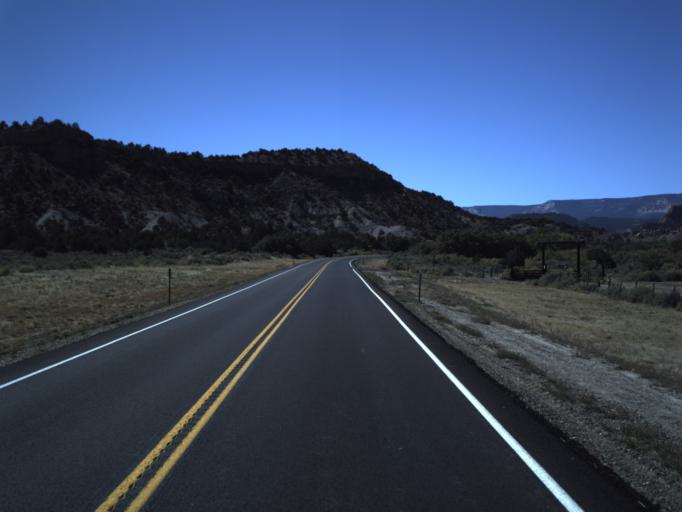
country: US
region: Utah
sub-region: Wayne County
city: Loa
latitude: 37.7739
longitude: -111.6461
